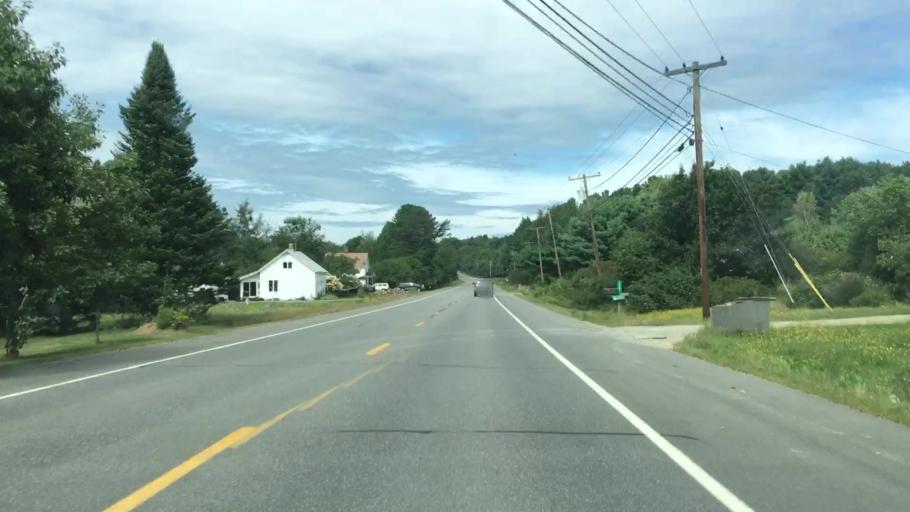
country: US
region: Maine
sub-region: Piscataquis County
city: Milo
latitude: 45.2730
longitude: -69.0006
